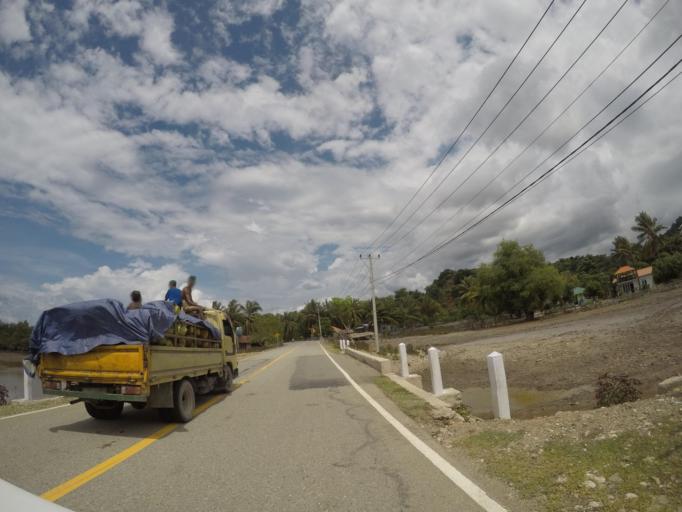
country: TL
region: Bobonaro
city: Maliana
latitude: -8.8307
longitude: 125.0590
